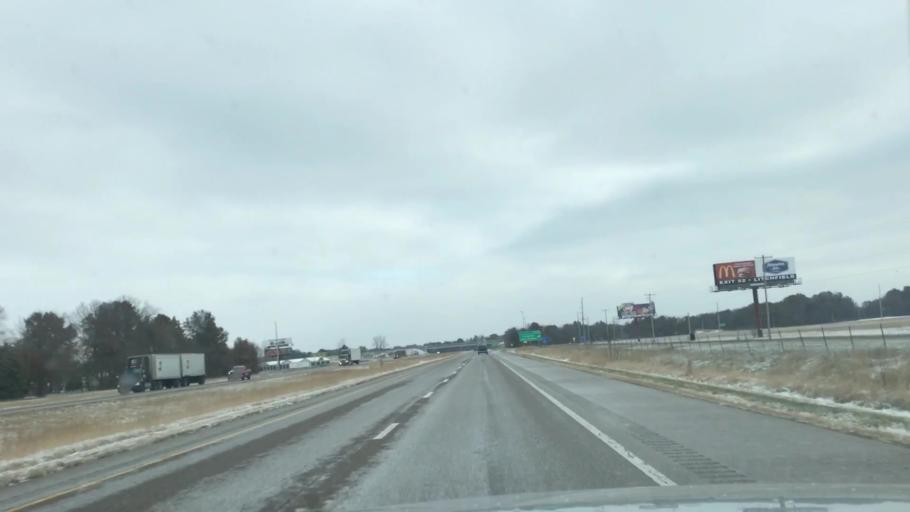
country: US
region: Illinois
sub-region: Macoupin County
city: Staunton
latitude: 38.9624
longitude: -89.7600
